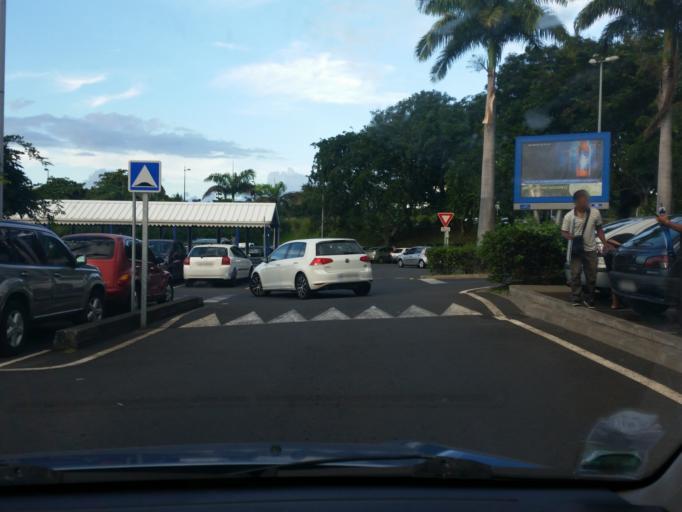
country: RE
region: Reunion
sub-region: Reunion
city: Sainte-Marie
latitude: -20.8933
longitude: 55.5006
